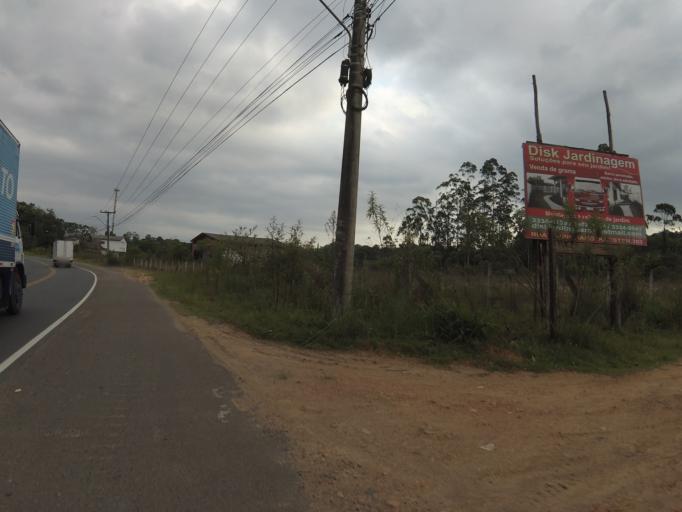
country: BR
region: Santa Catarina
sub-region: Indaial
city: Indaial
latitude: -26.8617
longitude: -49.1548
